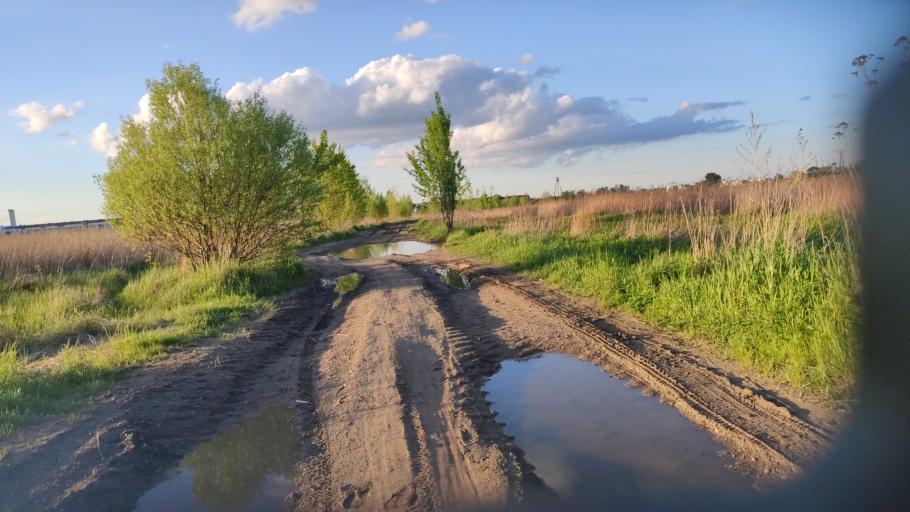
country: PL
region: Lower Silesian Voivodeship
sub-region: Powiat wroclawski
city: Zerniki Wroclawskie
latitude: 51.0505
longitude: 17.0383
